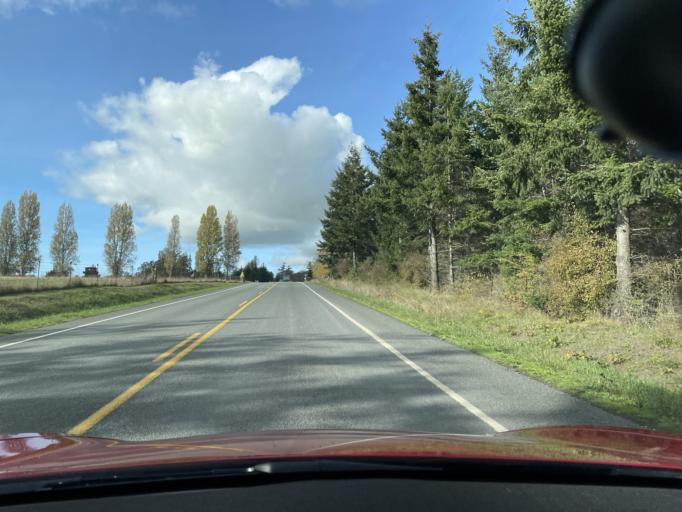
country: US
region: Washington
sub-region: San Juan County
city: Friday Harbor
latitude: 48.5108
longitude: -123.0291
